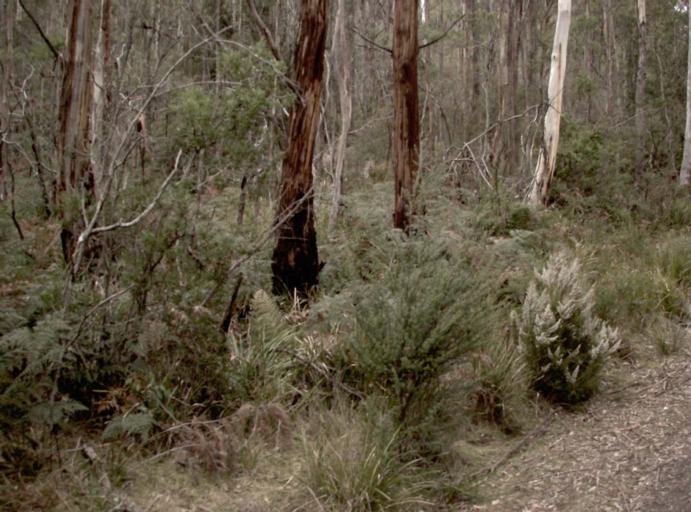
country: AU
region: Tasmania
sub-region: Launceston
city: Newstead
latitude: -41.3959
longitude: 147.3044
